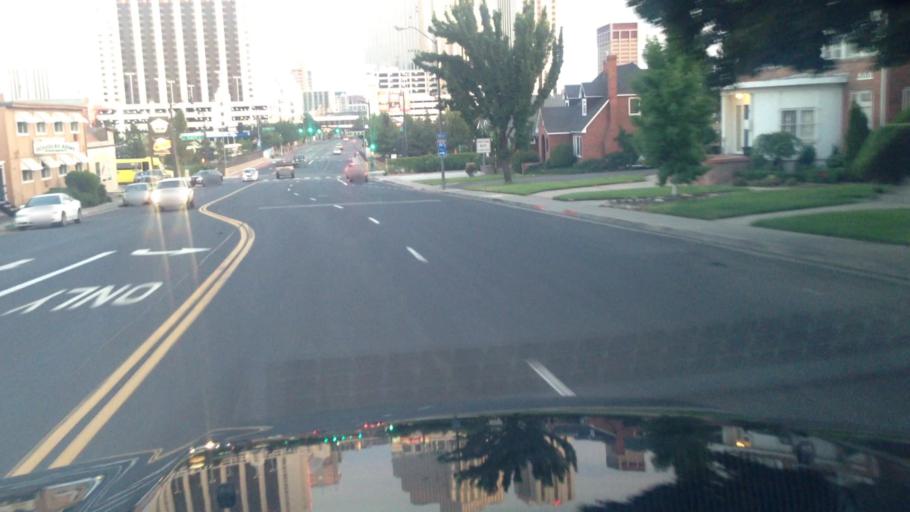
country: US
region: Nevada
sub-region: Washoe County
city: Reno
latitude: 39.5358
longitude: -119.8177
